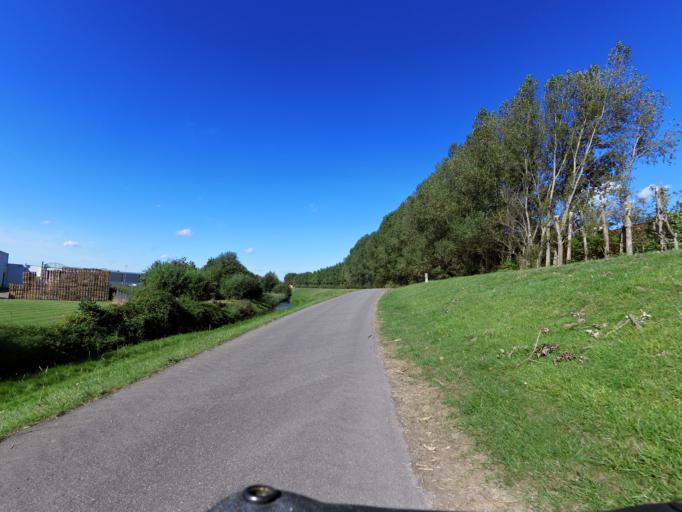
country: NL
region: South Holland
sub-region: Gemeente Zwijndrecht
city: Zwijndrecht
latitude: 51.7899
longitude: 4.6185
